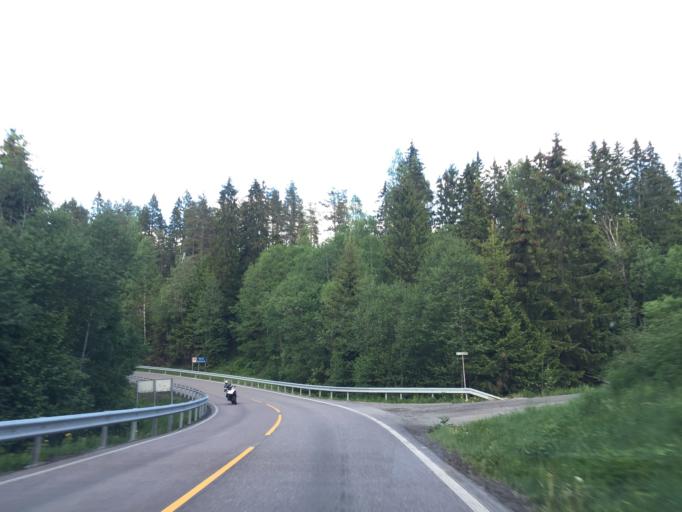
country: NO
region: Akershus
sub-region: Sorum
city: Sorumsand
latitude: 59.9649
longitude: 11.2135
